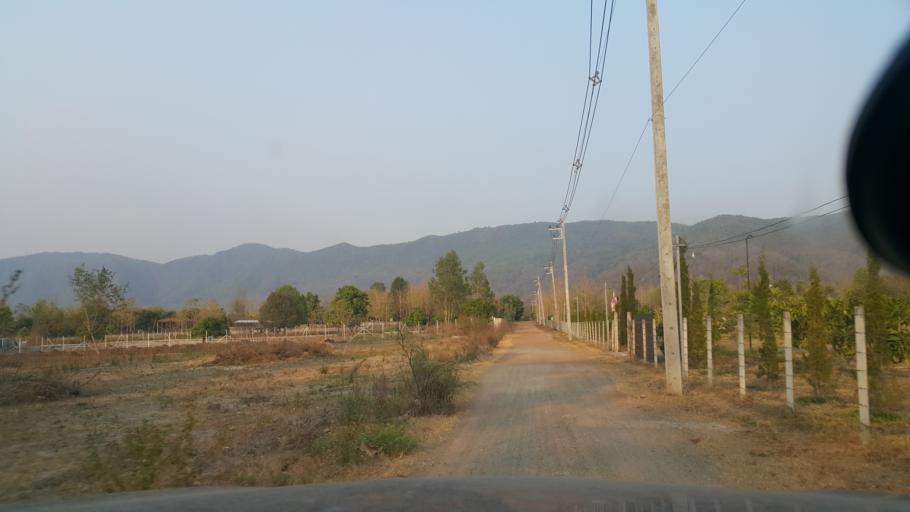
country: TH
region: Chiang Mai
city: Mae On
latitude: 18.7463
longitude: 99.2525
